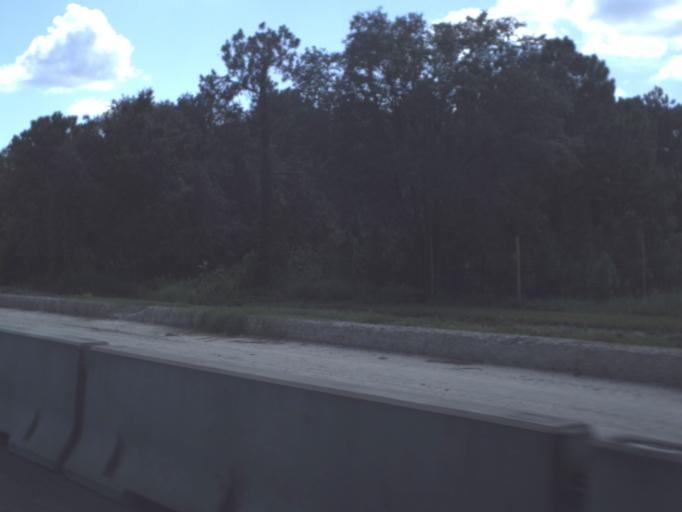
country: US
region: Florida
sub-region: Pasco County
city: Wesley Chapel
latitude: 28.2843
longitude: -82.3264
